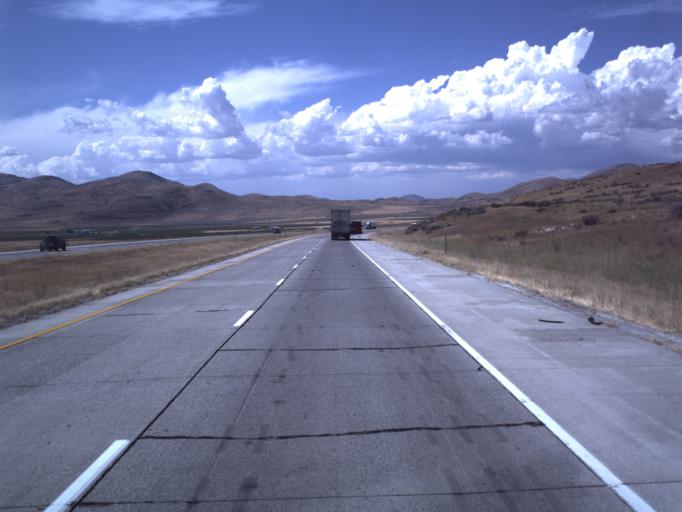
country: US
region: Utah
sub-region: Box Elder County
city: Tremonton
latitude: 41.7368
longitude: -112.2524
